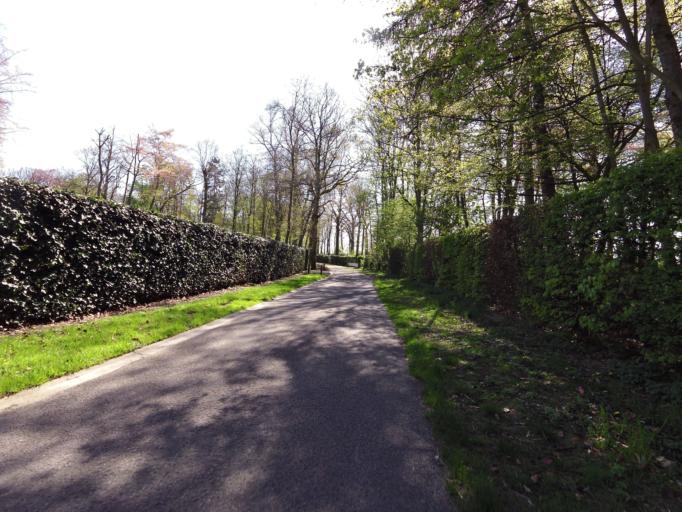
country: BE
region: Flanders
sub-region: Provincie West-Vlaanderen
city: Jabbeke
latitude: 51.1899
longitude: 3.0805
